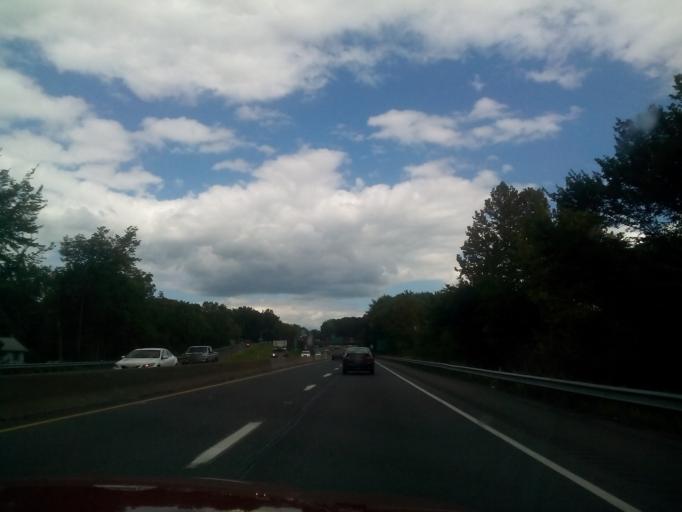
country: US
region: Pennsylvania
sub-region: Monroe County
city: East Stroudsburg
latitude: 40.9885
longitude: -75.1793
